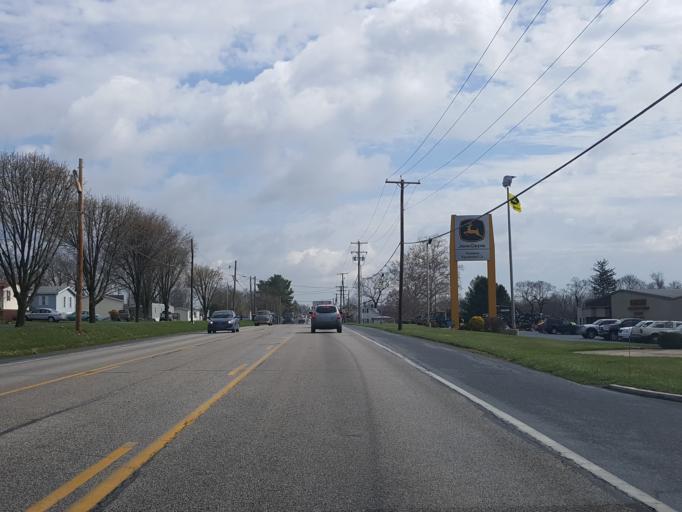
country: US
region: Pennsylvania
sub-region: Lebanon County
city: Avon
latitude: 40.3591
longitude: -76.3620
